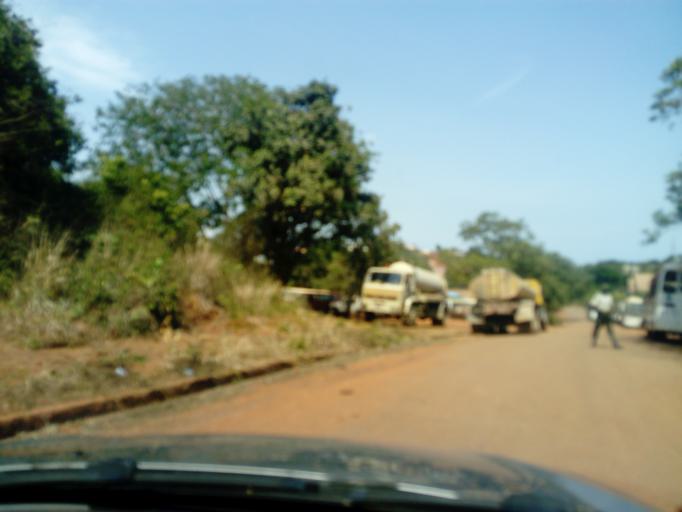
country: GH
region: Central
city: Cape Coast
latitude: 5.1077
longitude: -1.2817
